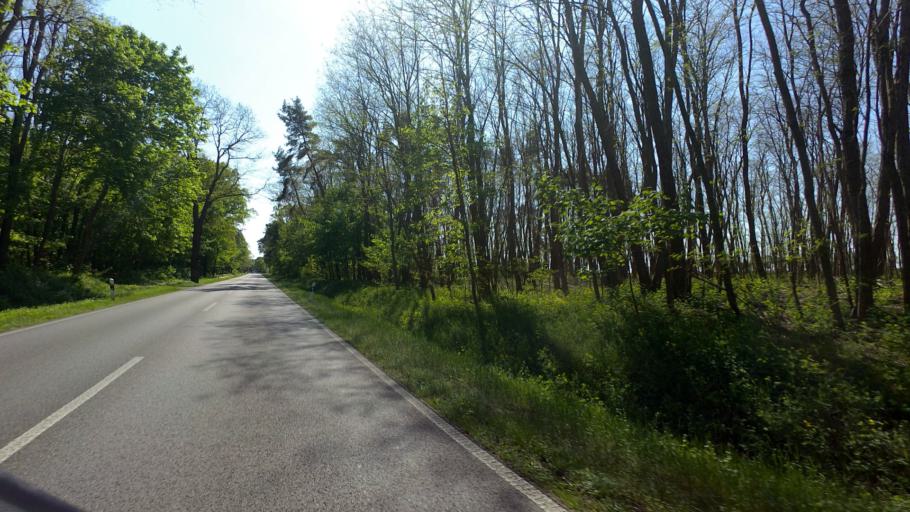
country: DE
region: Brandenburg
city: Tauche
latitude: 52.1242
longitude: 14.1951
